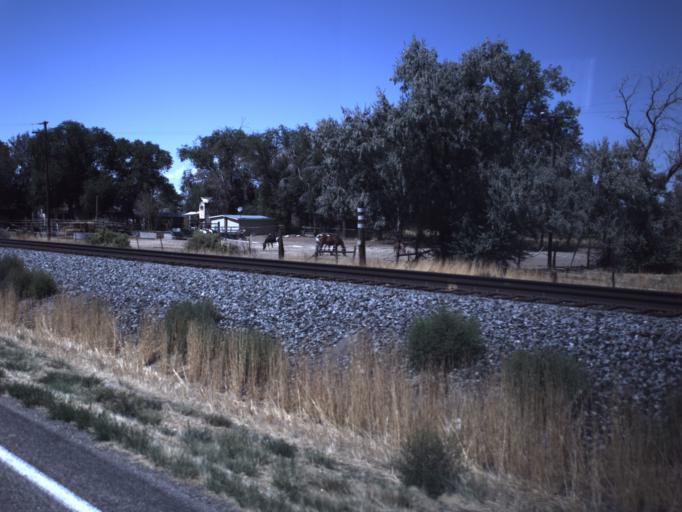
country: US
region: Utah
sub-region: Millard County
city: Delta
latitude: 39.5343
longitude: -112.2884
